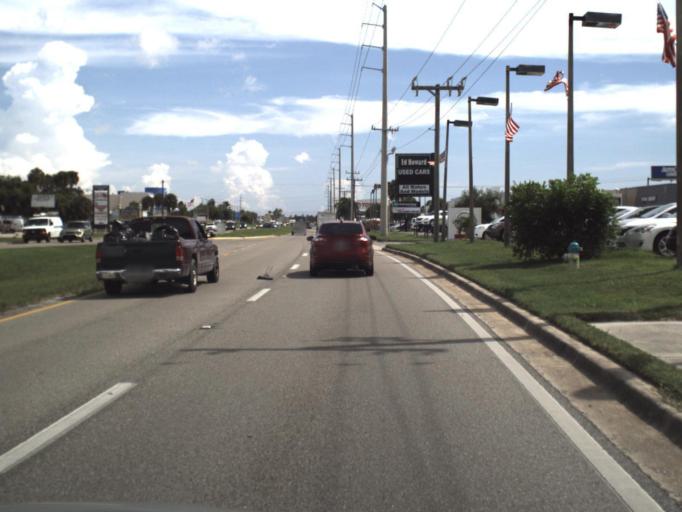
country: US
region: Florida
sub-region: Sarasota County
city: Venice
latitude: 27.0911
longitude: -82.4328
